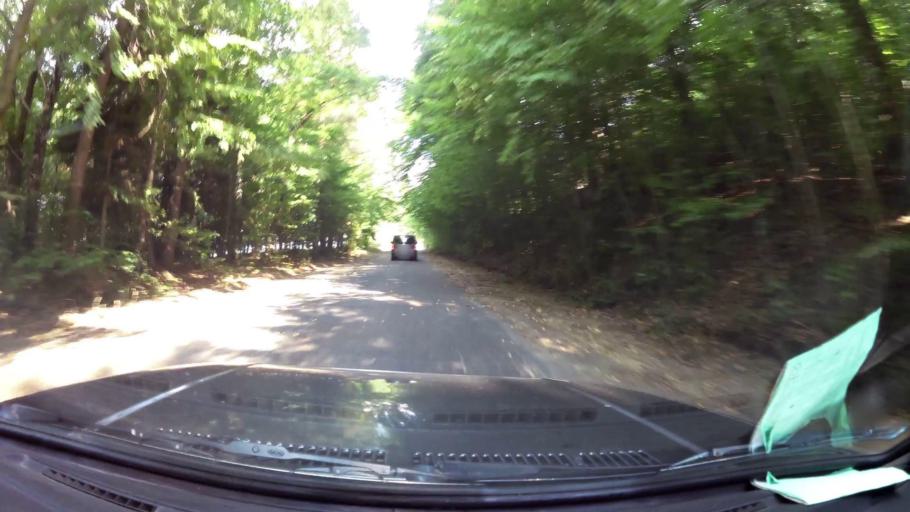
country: PL
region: West Pomeranian Voivodeship
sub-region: Powiat koszalinski
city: Bobolice
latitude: 54.1041
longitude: 16.4980
